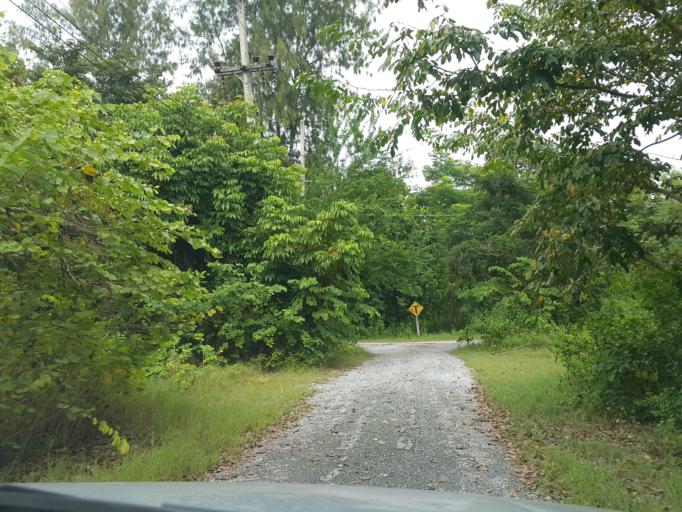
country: TH
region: Chiang Mai
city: San Kamphaeng
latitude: 18.8043
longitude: 99.1333
